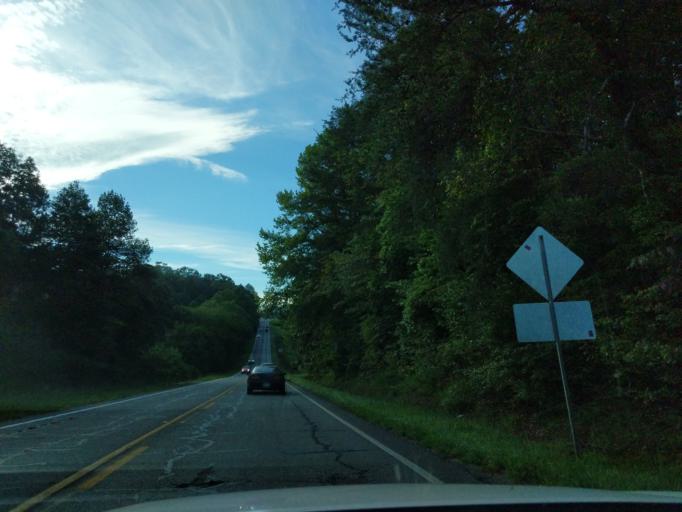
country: US
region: Georgia
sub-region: Fannin County
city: Blue Ridge
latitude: 34.8912
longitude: -84.3486
